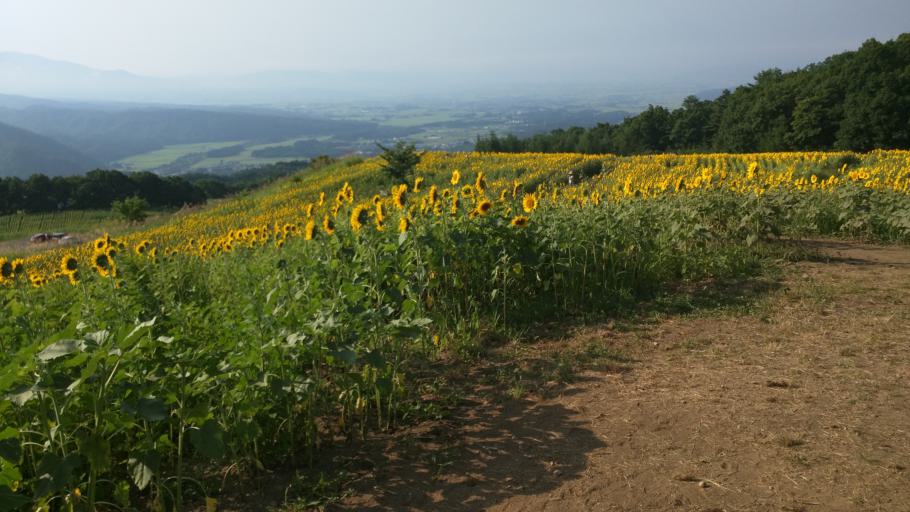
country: JP
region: Fukushima
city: Kitakata
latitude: 37.7492
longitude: 139.8661
